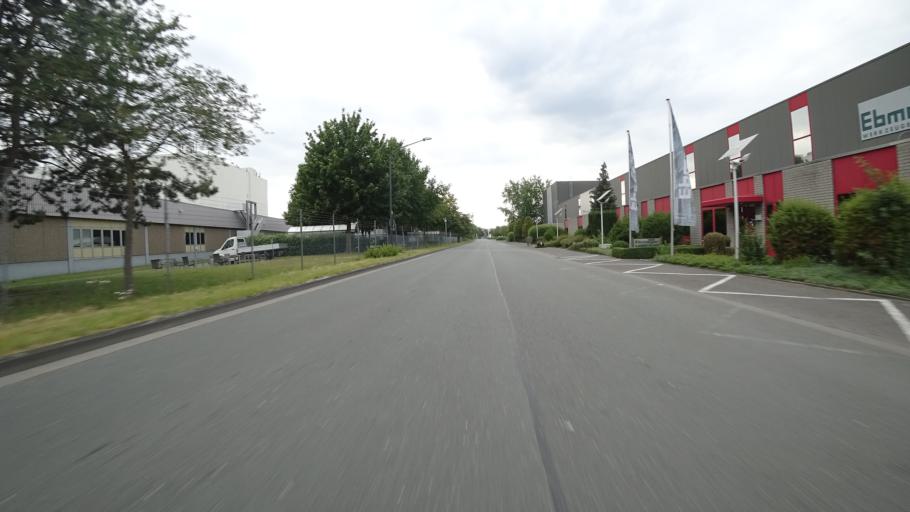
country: DE
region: North Rhine-Westphalia
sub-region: Regierungsbezirk Detmold
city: Verl
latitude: 51.8866
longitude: 8.4469
